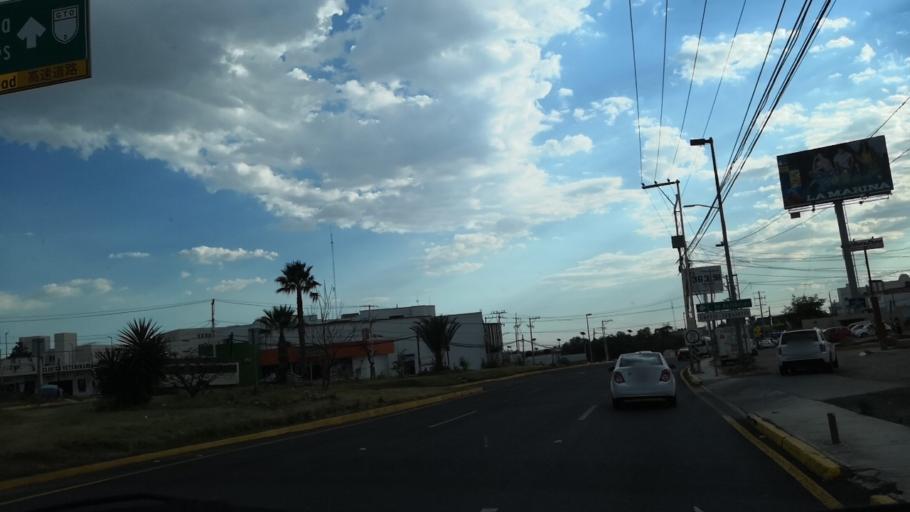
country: MX
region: Guanajuato
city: Marfil
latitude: 20.9868
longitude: -101.2861
